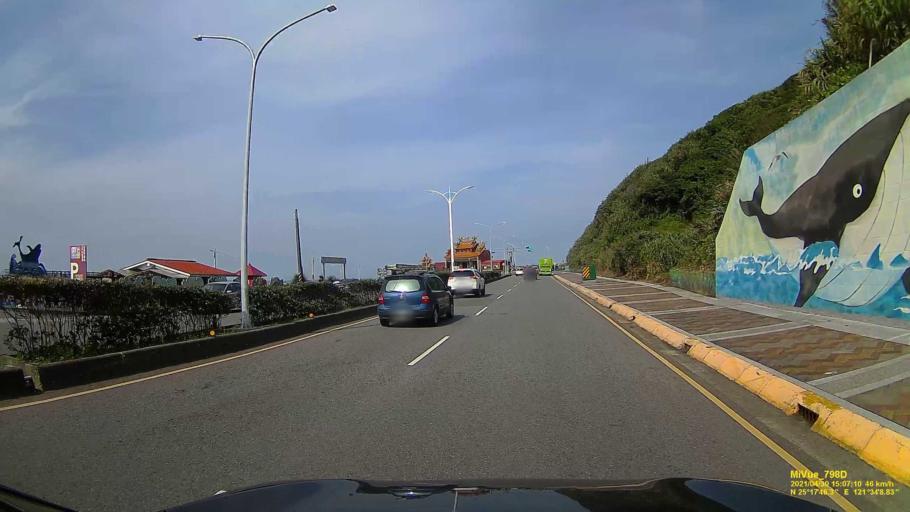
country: TW
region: Taiwan
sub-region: Keelung
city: Keelung
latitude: 25.2963
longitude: 121.5694
